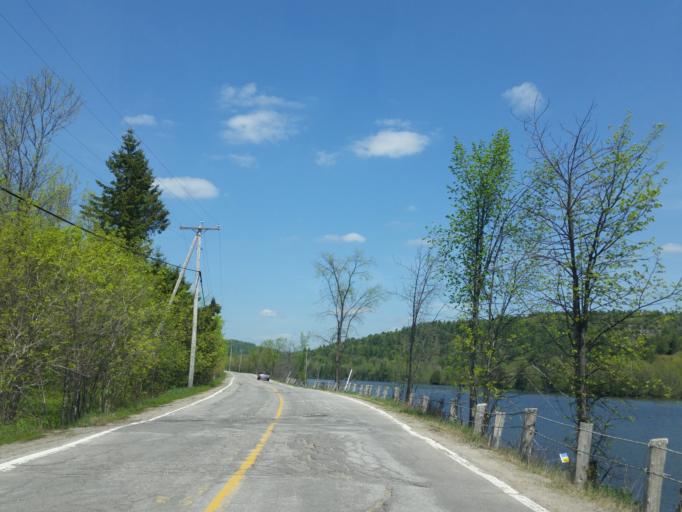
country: CA
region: Quebec
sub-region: Outaouais
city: Wakefield
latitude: 45.6118
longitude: -75.8977
